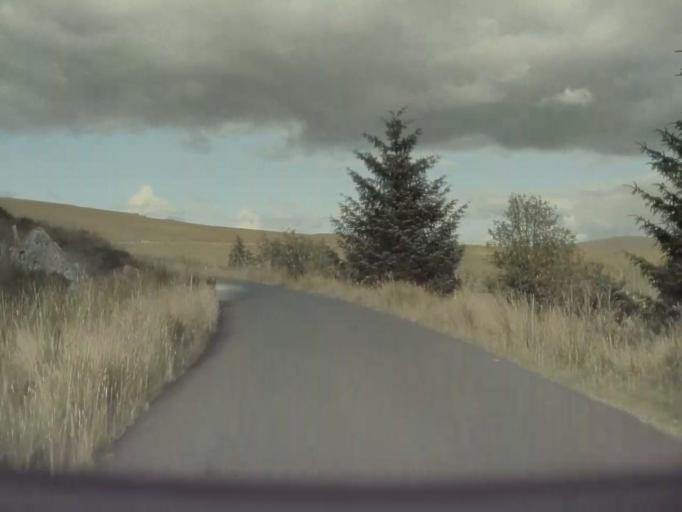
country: IE
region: Leinster
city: Oldbawn
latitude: 53.1024
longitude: -6.3433
